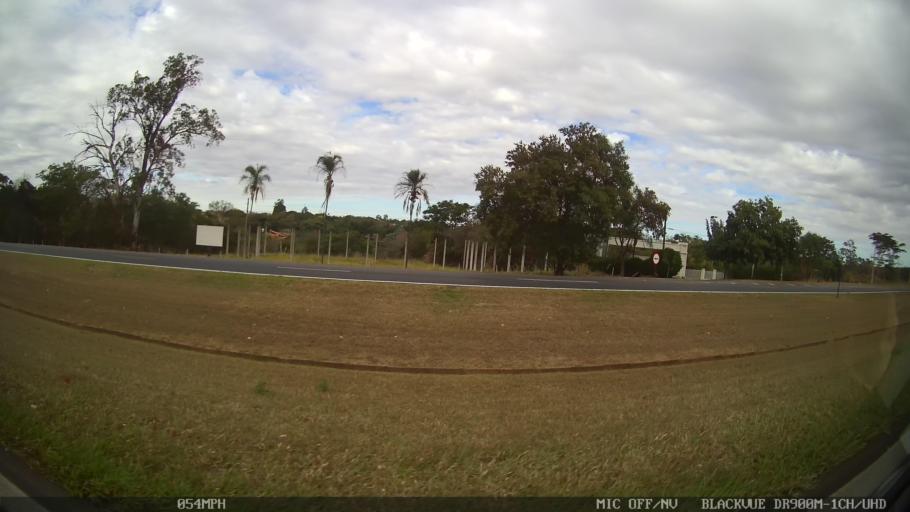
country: BR
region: Sao Paulo
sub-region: Sao Jose Do Rio Preto
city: Sao Jose do Rio Preto
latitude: -20.8135
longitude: -49.4765
